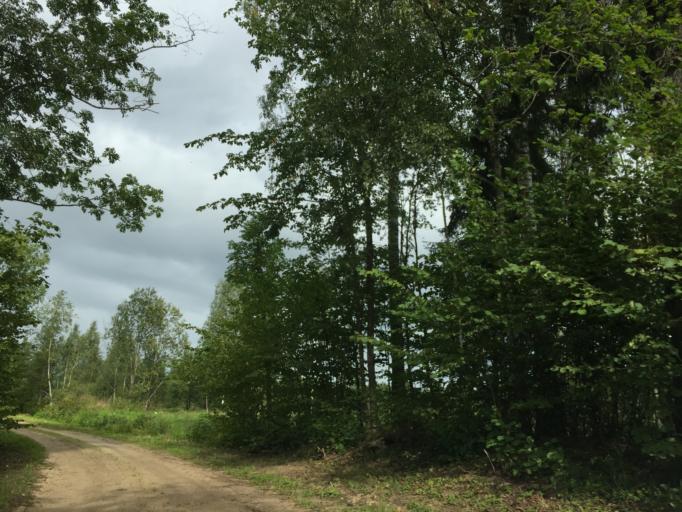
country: LV
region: Pargaujas
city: Stalbe
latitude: 57.5021
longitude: 24.9183
